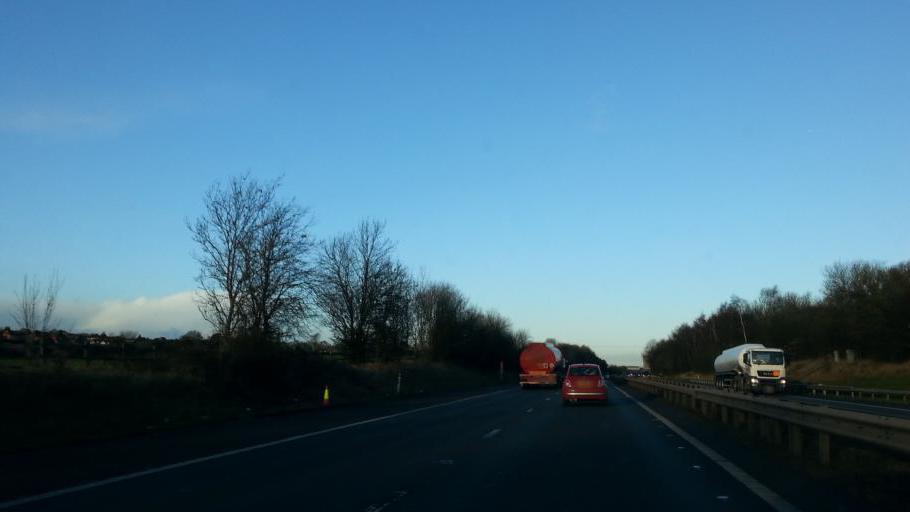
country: GB
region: England
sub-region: Staffordshire
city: Fazeley
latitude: 52.6125
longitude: -1.6345
